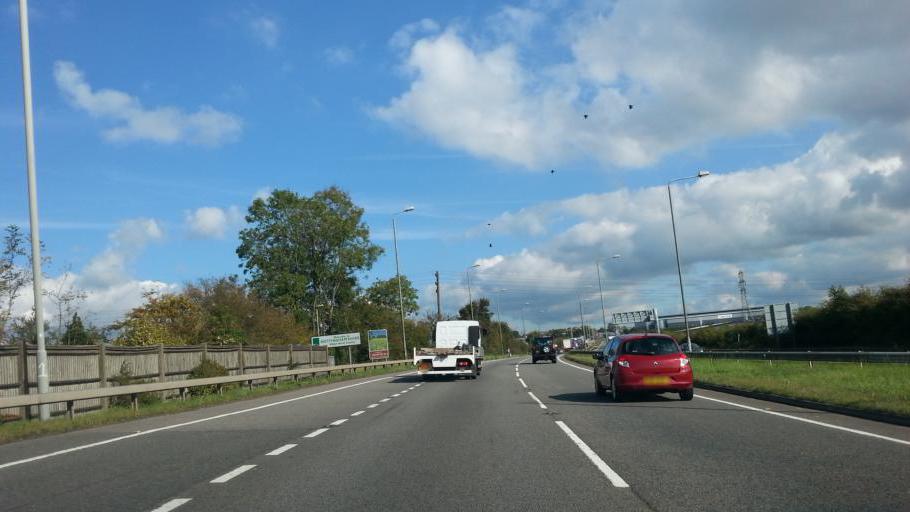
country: GB
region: England
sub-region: Derbyshire
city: Pinxton
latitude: 53.1104
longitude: -1.3107
